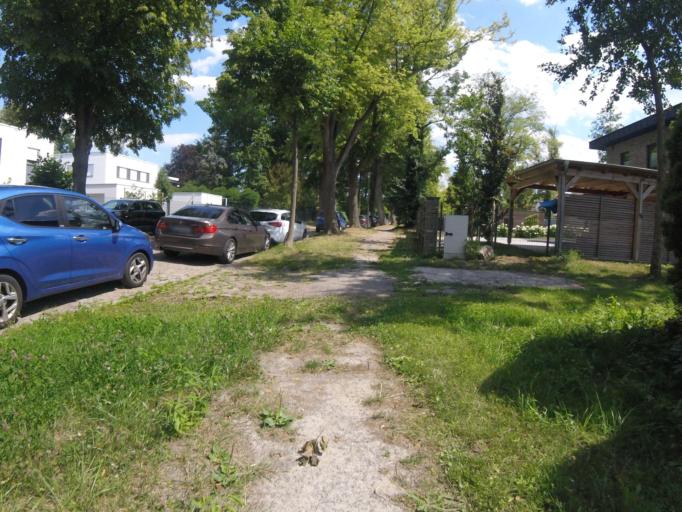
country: DE
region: Brandenburg
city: Wildau
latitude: 52.3391
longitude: 13.6401
